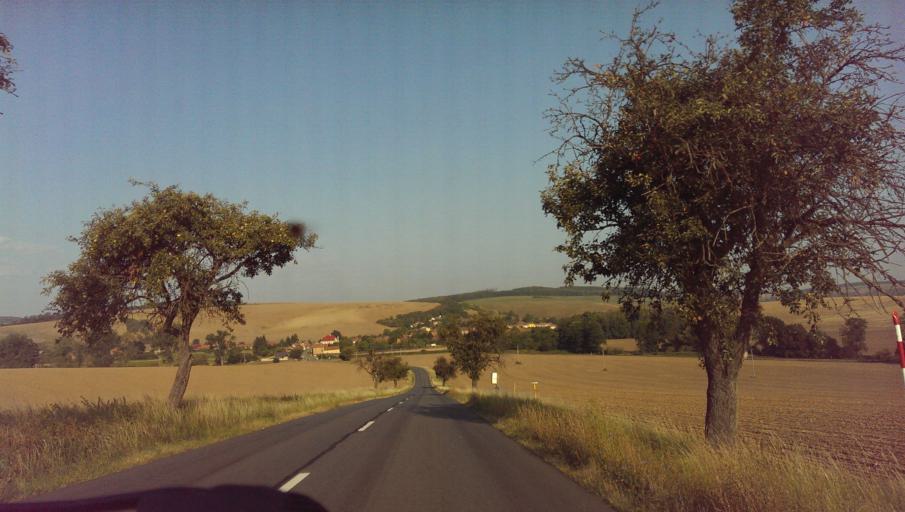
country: CZ
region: Zlin
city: Korycany
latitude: 49.1092
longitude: 17.1473
